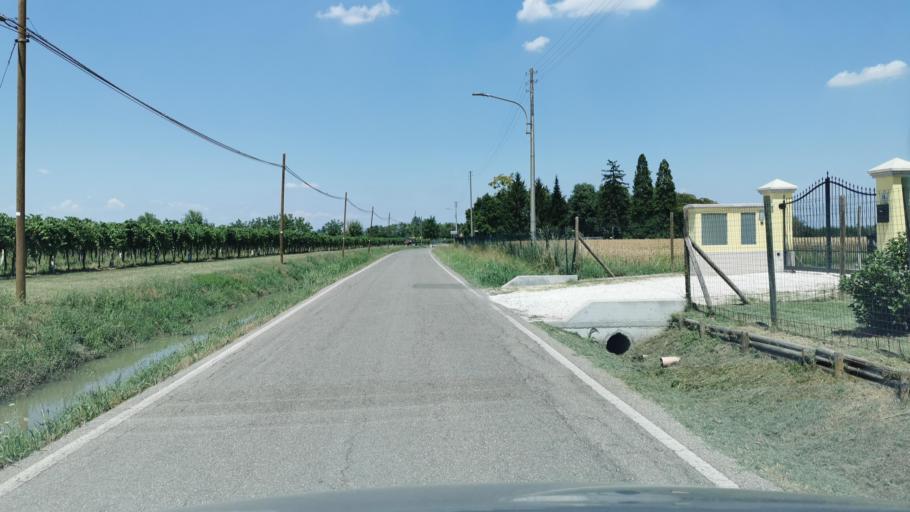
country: IT
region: Emilia-Romagna
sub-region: Provincia di Modena
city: Fossoli
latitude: 44.8219
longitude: 10.8982
